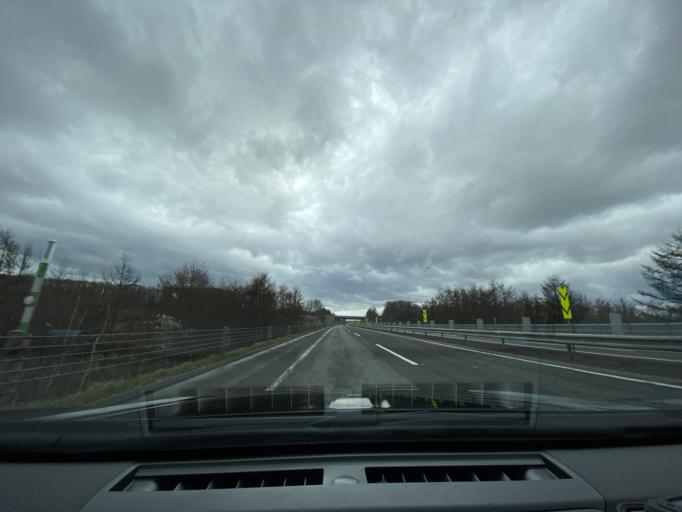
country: JP
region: Hokkaido
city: Fukagawa
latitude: 43.6338
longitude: 141.9855
